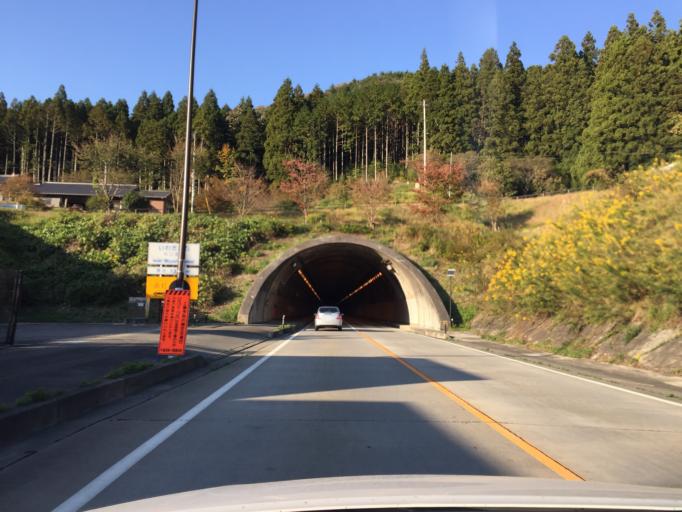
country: JP
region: Fukushima
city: Iwaki
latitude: 37.0844
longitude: 140.7814
